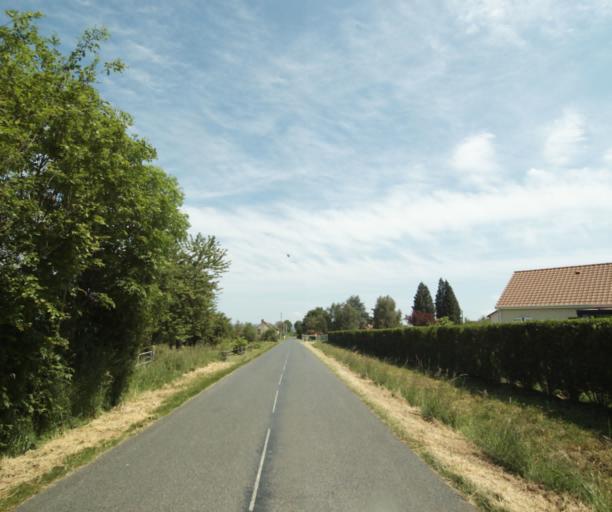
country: FR
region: Bourgogne
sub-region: Departement de Saone-et-Loire
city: Gueugnon
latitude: 46.5781
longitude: 4.1373
